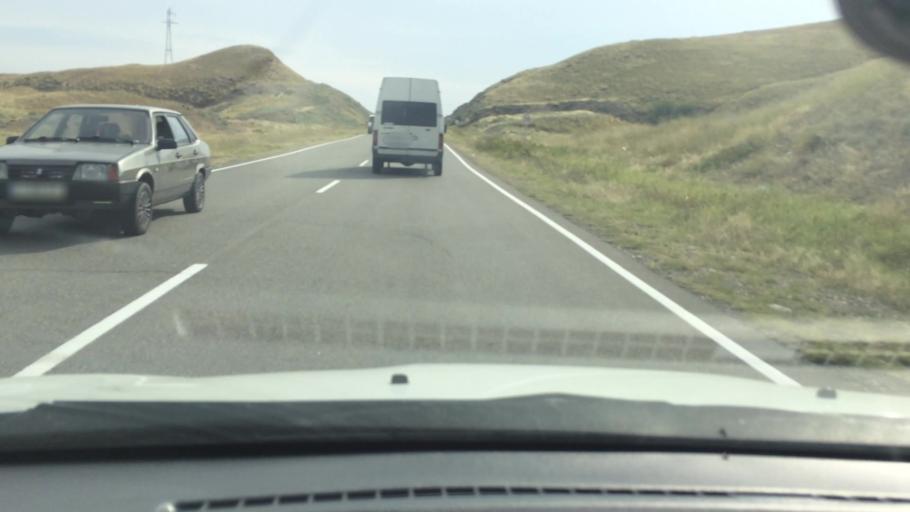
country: GE
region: Kvemo Kartli
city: Rust'avi
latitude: 41.5255
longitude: 44.9881
